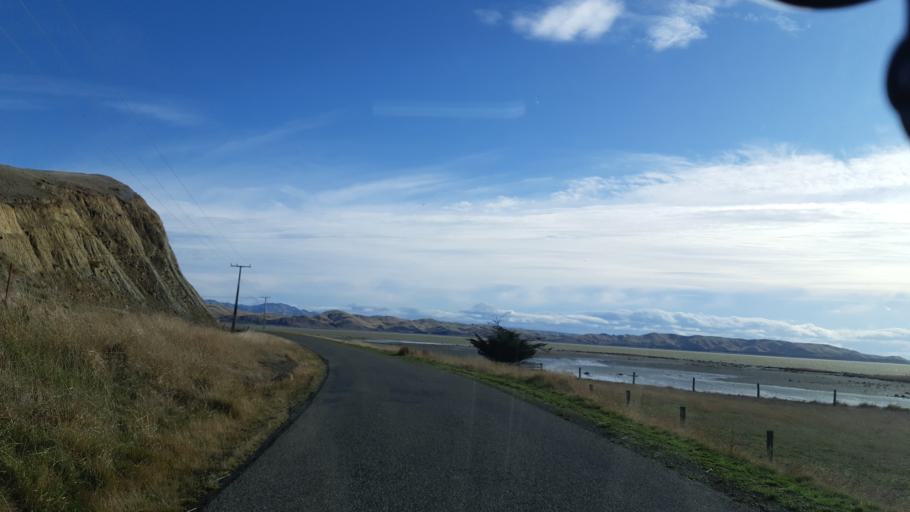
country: NZ
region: Marlborough
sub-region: Marlborough District
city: Blenheim
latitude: -41.7384
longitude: 174.1733
